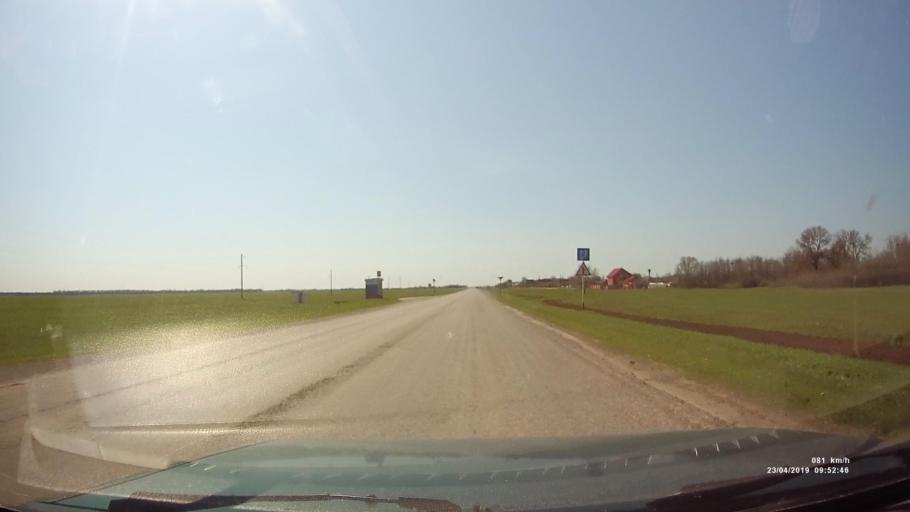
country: RU
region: Rostov
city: Orlovskiy
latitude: 46.8408
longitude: 42.0473
